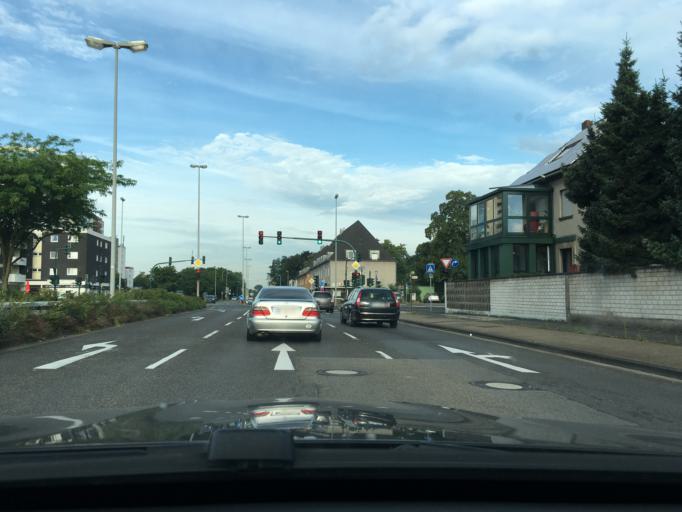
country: DE
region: North Rhine-Westphalia
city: Opladen
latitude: 51.0342
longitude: 7.0237
